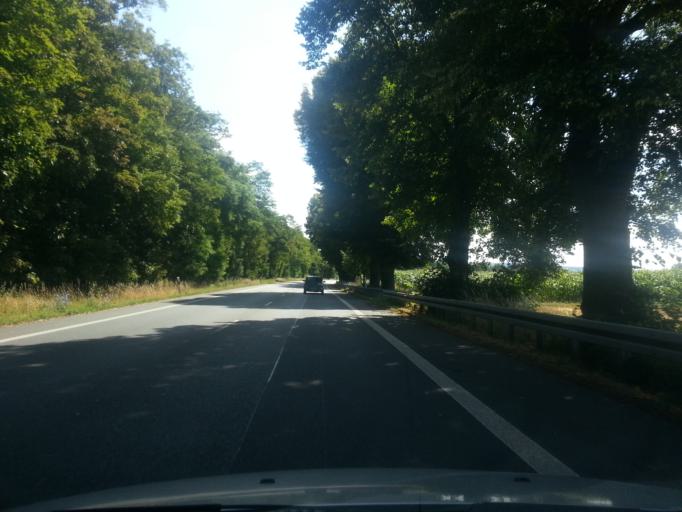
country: DE
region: Hesse
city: Dieburg
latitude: 49.8872
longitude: 8.8771
